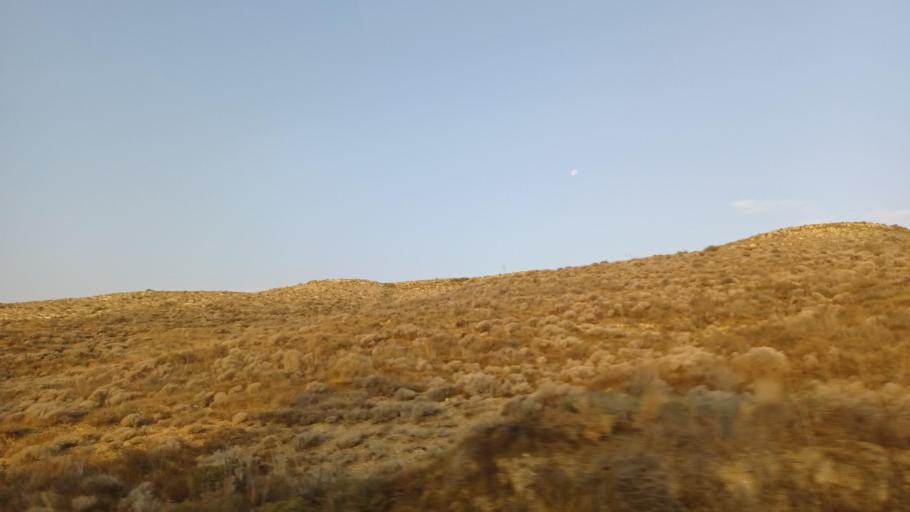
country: CY
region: Larnaka
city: Athienou
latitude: 35.0097
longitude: 33.5281
